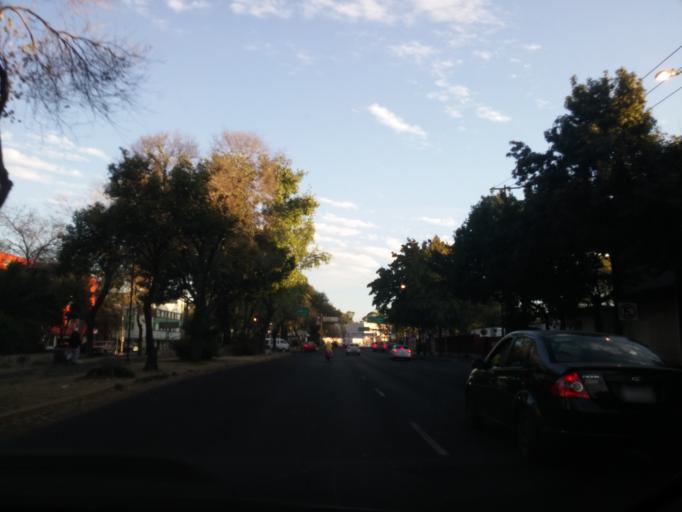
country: MX
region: Mexico City
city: Cuauhtemoc
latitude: 19.4585
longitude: -99.1693
